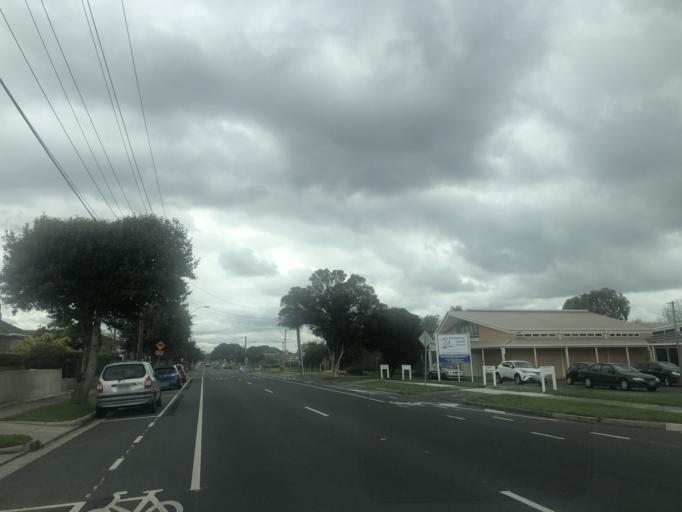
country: AU
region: Victoria
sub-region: Greater Dandenong
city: Dandenong North
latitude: -37.9752
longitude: 145.2101
